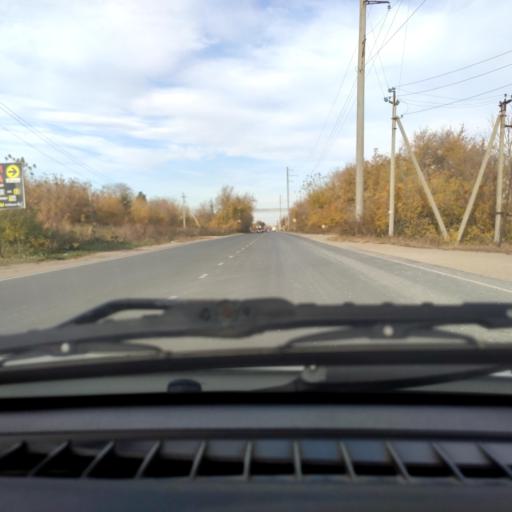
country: RU
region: Samara
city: Zhigulevsk
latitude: 53.5262
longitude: 49.4815
